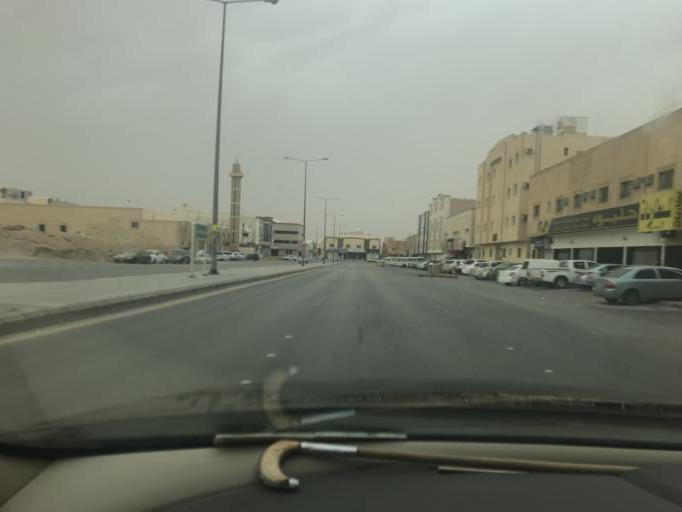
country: SA
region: Ar Riyad
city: Riyadh
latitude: 24.7889
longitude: 46.6928
